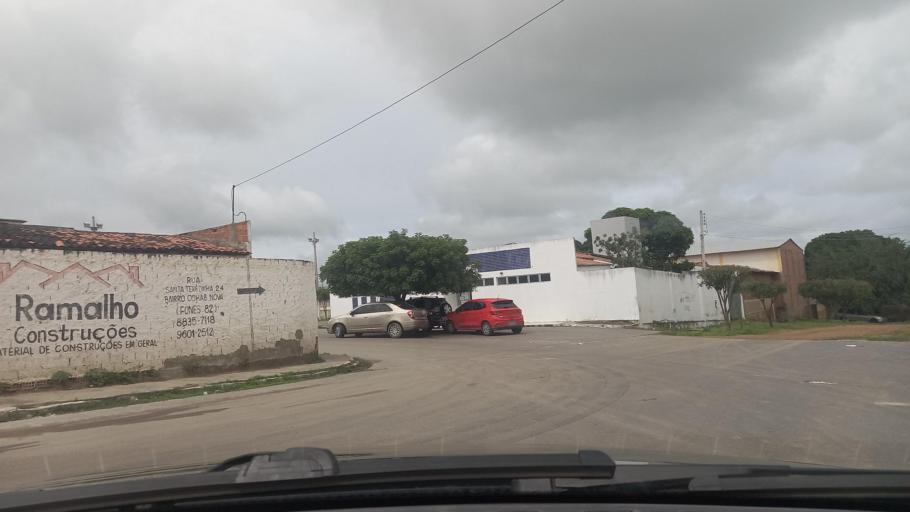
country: BR
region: Alagoas
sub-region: Delmiro Gouveia
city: Delmiro Gouveia
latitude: -9.3924
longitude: -37.9983
